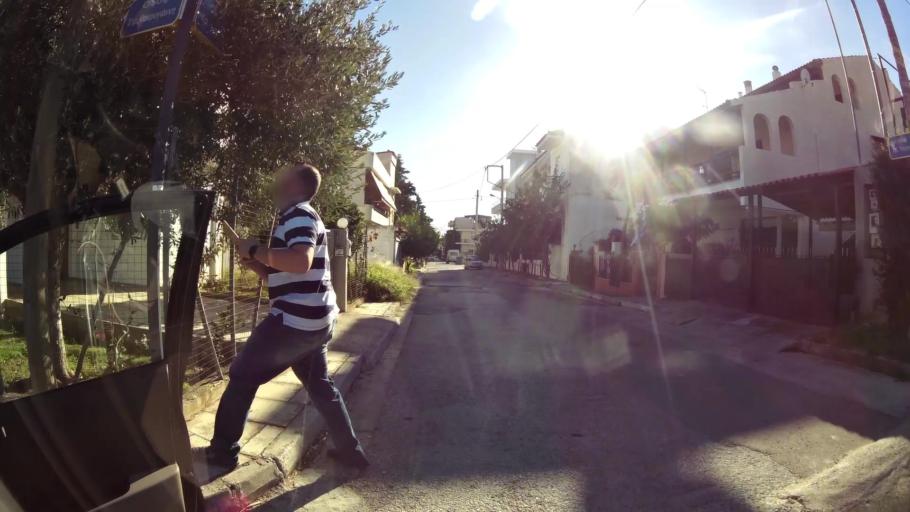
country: GR
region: Attica
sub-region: Nomarchia Anatolikis Attikis
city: Koropi
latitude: 37.8979
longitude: 23.8619
